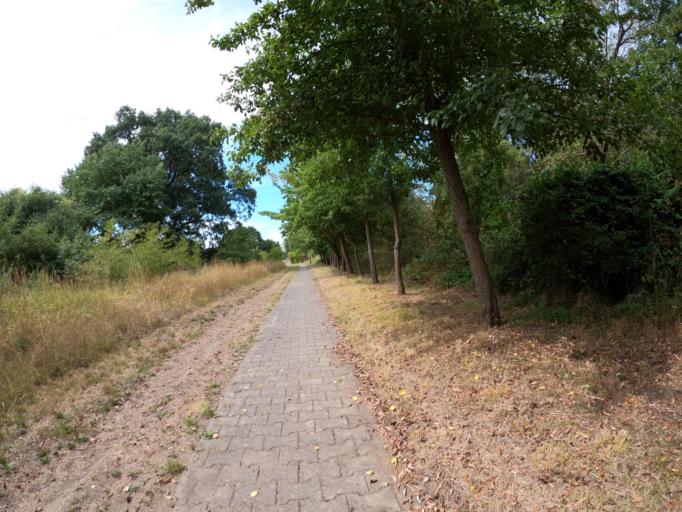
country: DE
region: Mecklenburg-Vorpommern
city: Loitz
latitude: 53.4234
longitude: 13.4338
